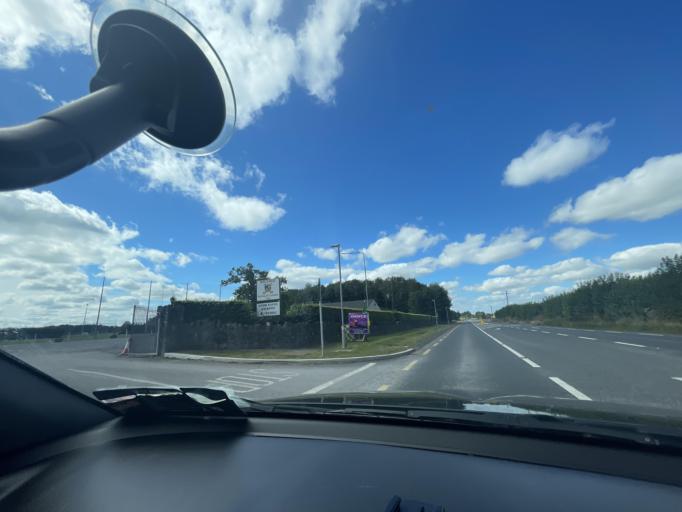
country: IE
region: Leinster
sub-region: An Mhi
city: Newtown Trim
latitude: 53.5237
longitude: -6.6601
